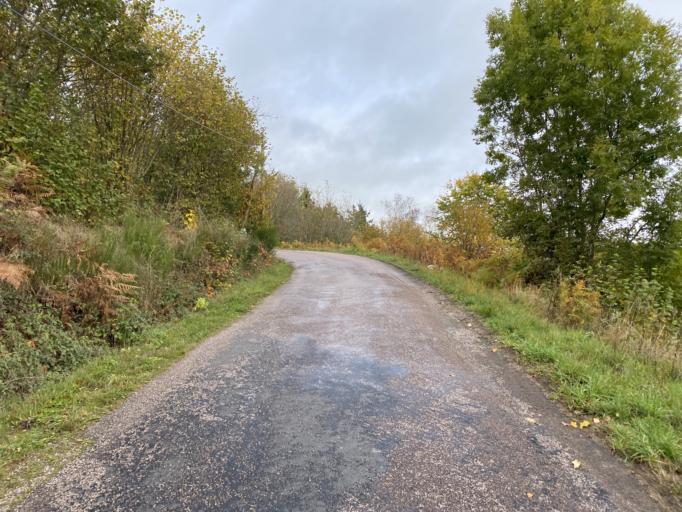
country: FR
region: Bourgogne
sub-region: Departement de la Cote-d'Or
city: Saulieu
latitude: 47.2625
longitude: 4.1712
